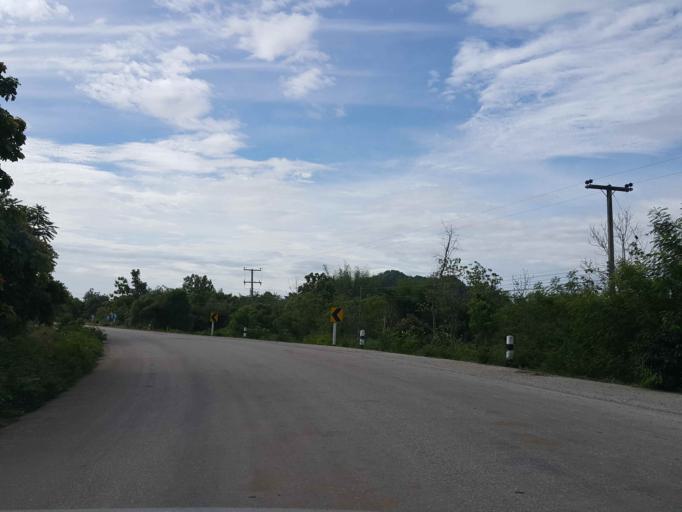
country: TH
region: Sukhothai
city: Thung Saliam
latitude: 17.2719
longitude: 99.5312
